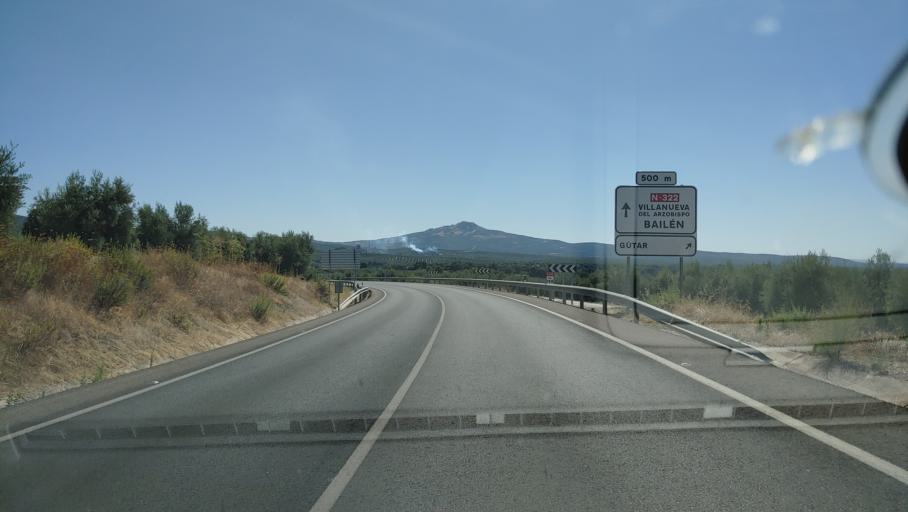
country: ES
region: Andalusia
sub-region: Provincia de Jaen
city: Campina
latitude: 38.2200
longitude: -2.9748
